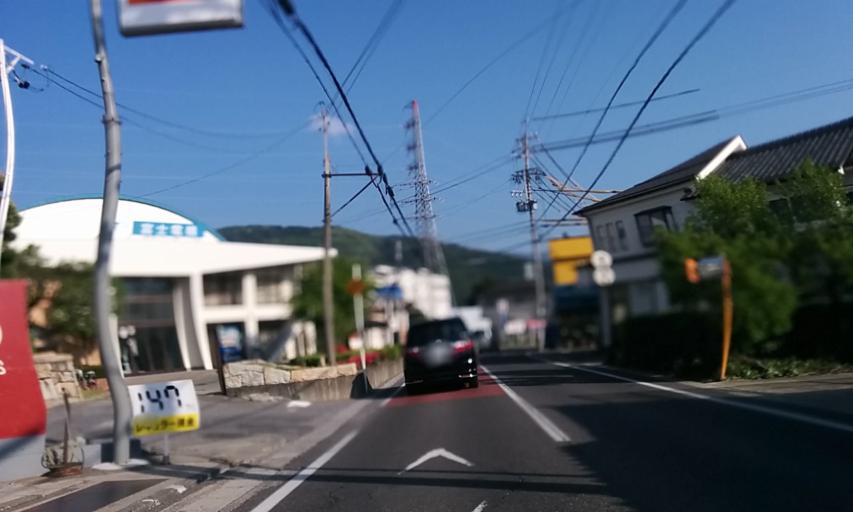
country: JP
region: Nagano
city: Matsumoto
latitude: 36.2251
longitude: 137.9850
